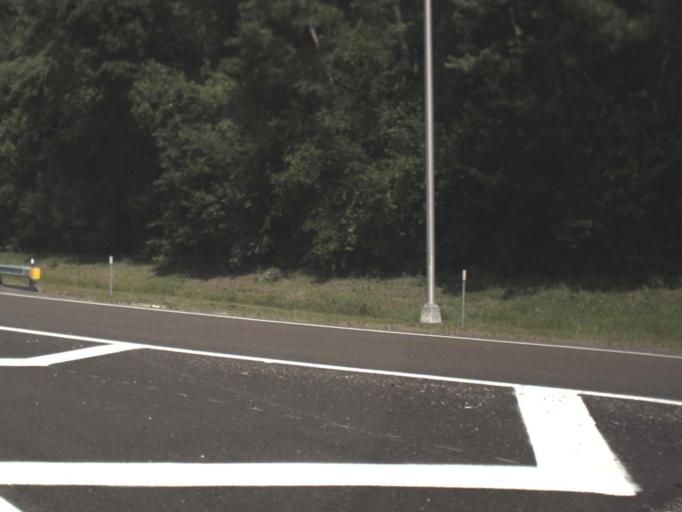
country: US
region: Florida
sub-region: Duval County
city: Jacksonville
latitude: 30.3154
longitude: -81.7679
